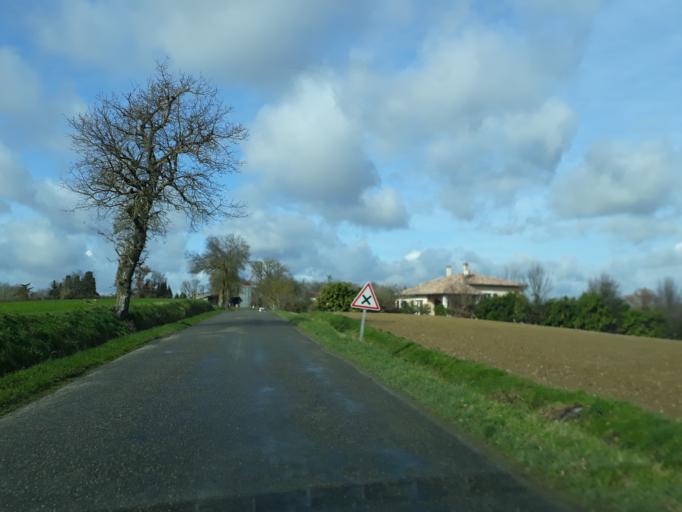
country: FR
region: Midi-Pyrenees
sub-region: Departement du Gers
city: Gimont
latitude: 43.6384
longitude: 1.0032
